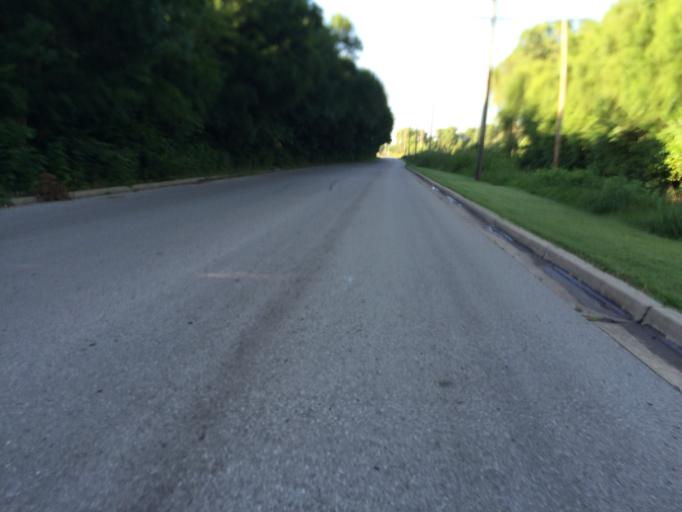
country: US
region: Oklahoma
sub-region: Cleveland County
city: Norman
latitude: 35.1789
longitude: -97.4503
